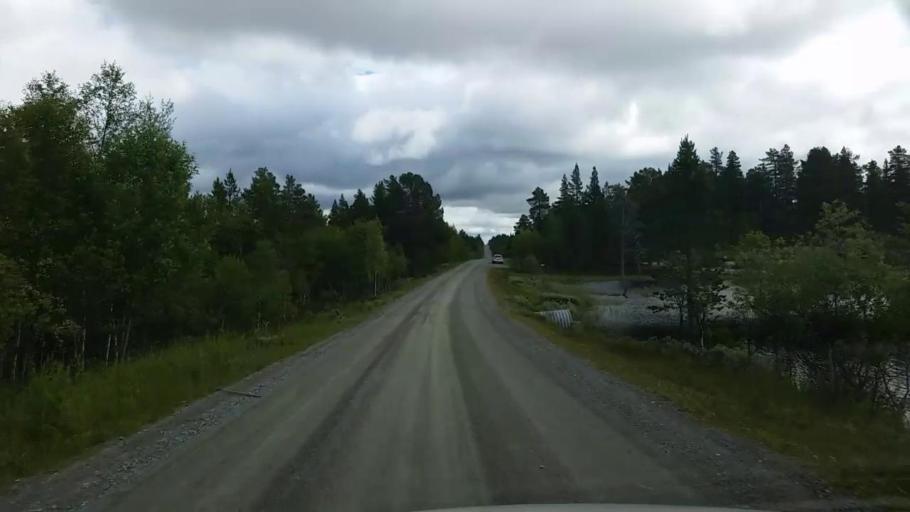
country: NO
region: Hedmark
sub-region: Engerdal
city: Engerdal
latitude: 62.3459
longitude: 12.5960
